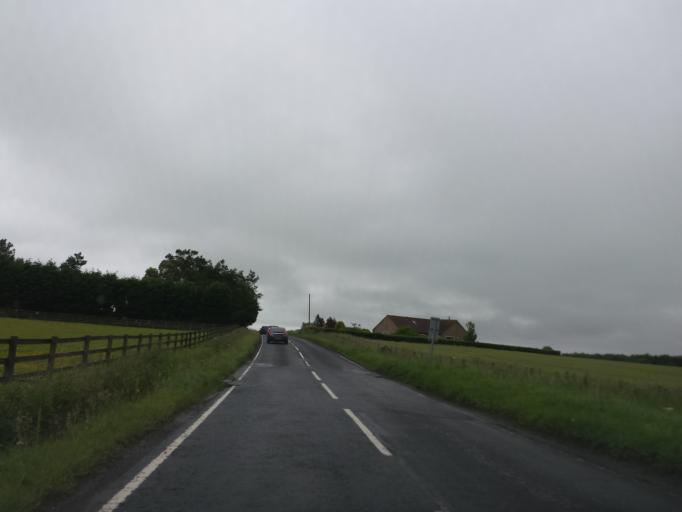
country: GB
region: Scotland
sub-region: Fife
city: Strathkinness
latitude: 56.2614
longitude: -2.8554
